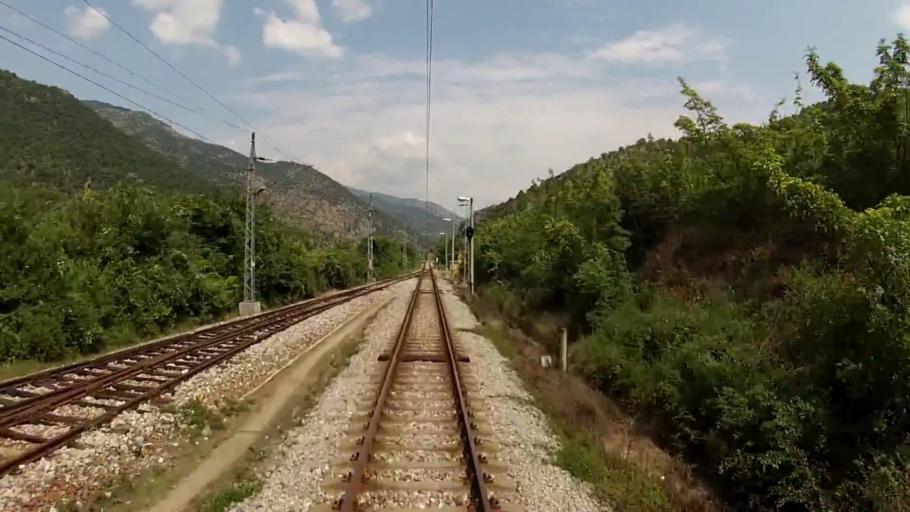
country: BG
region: Blagoevgrad
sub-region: Obshtina Kresna
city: Kresna
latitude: 41.7405
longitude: 23.1600
